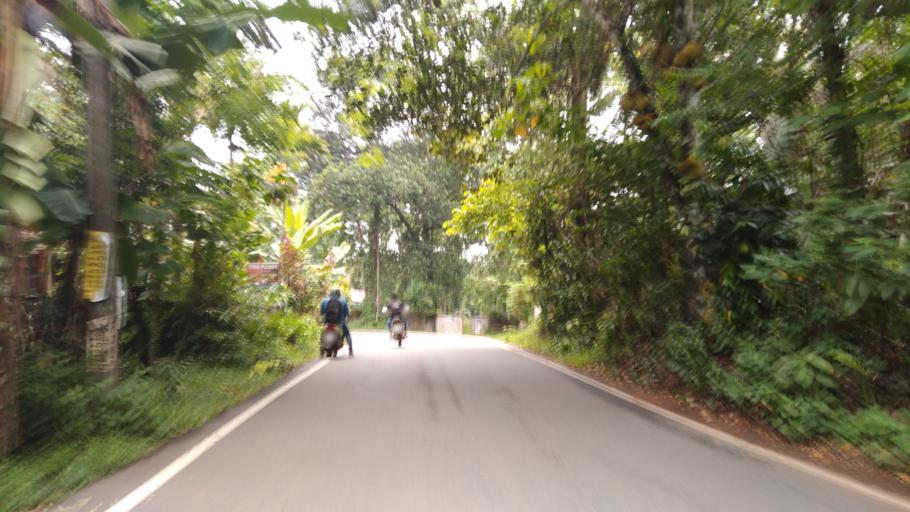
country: IN
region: Kerala
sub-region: Ernakulam
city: Perumpavur
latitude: 10.1233
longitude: 76.5458
